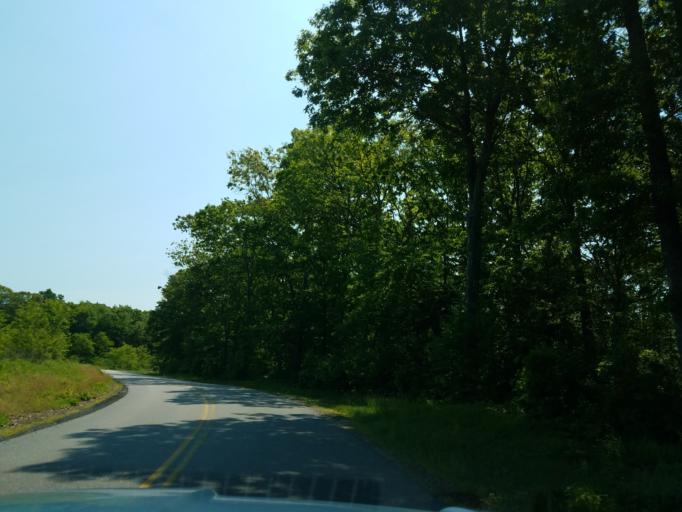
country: US
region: Connecticut
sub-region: New London County
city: Montville Center
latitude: 41.4971
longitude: -72.2197
